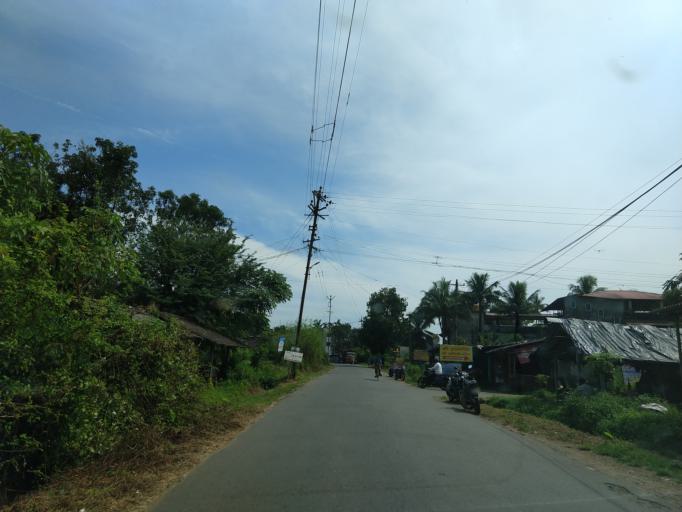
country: IN
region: Maharashtra
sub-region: Sindhudurg
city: Savantvadi
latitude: 15.9770
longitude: 73.7865
